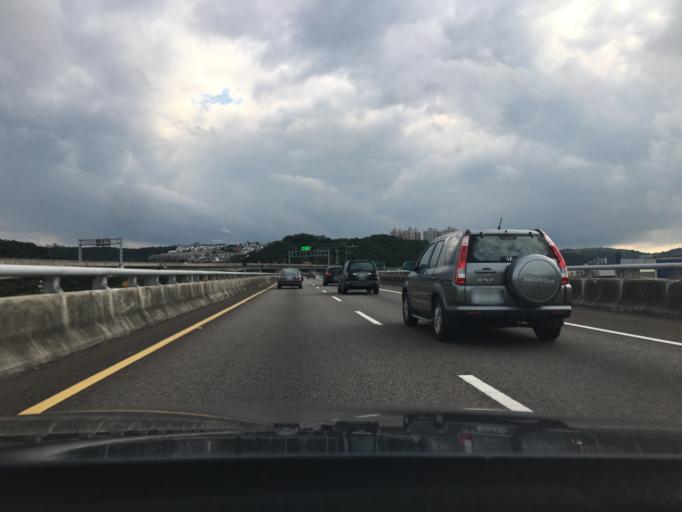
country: TW
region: Taiwan
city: Daxi
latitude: 24.9102
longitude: 121.1647
